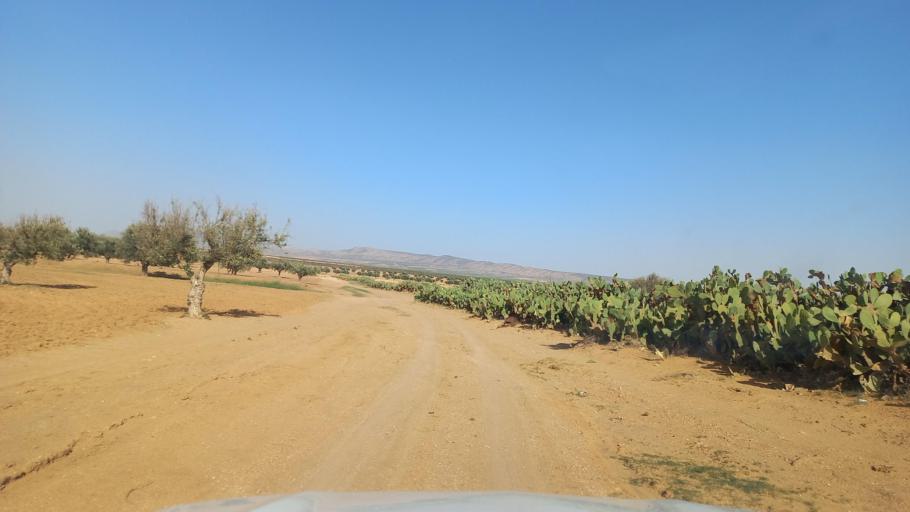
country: TN
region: Al Qasrayn
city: Sbiba
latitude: 35.3224
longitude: 9.0224
